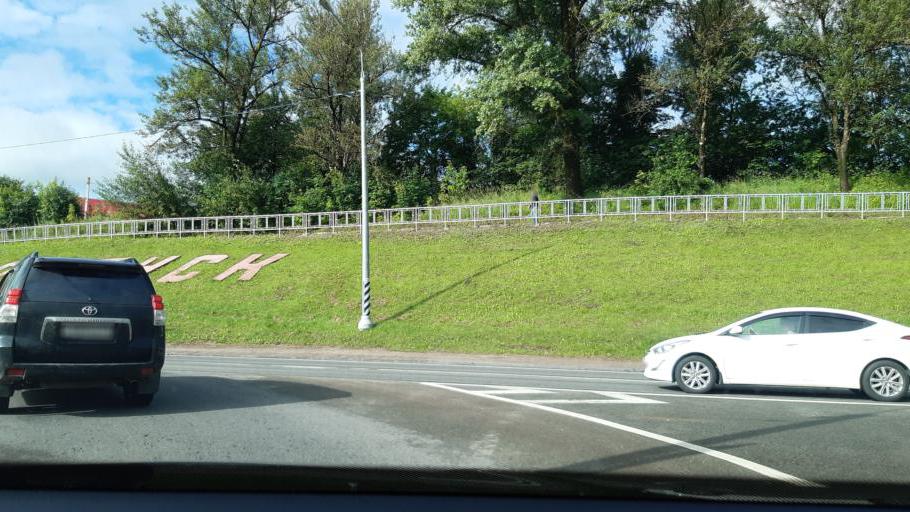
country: RU
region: Smolensk
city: Smolensk
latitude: 54.7567
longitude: 32.0715
